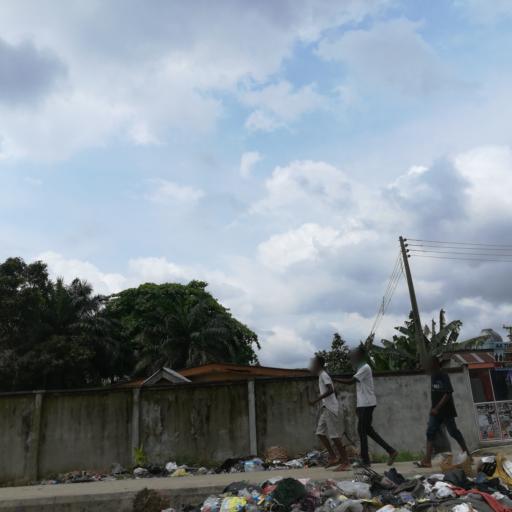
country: NG
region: Rivers
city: Port Harcourt
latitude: 4.8469
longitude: 7.0644
